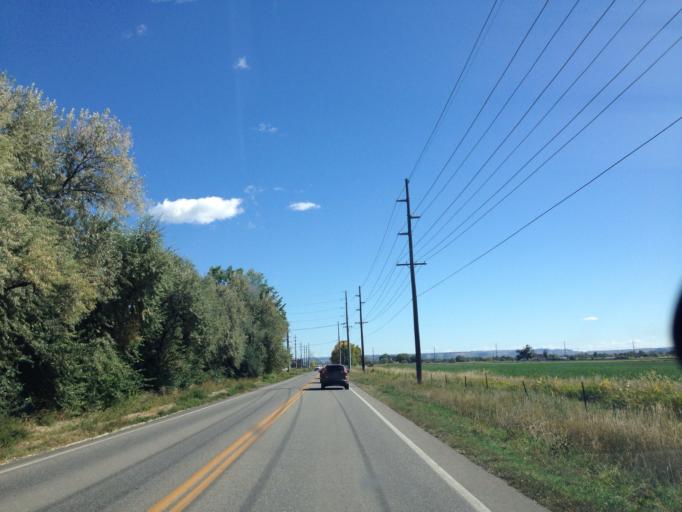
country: US
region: Montana
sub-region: Yellowstone County
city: Billings
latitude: 45.7841
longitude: -108.6271
